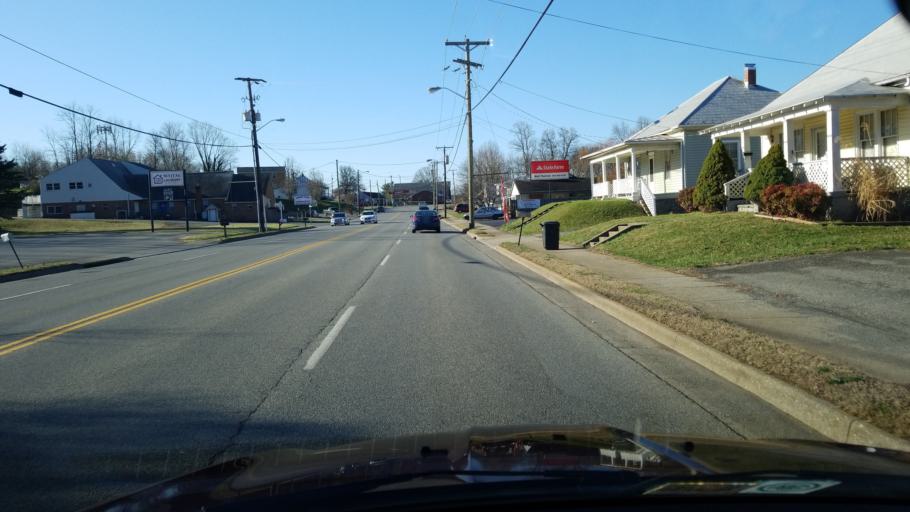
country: US
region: Virginia
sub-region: Franklin County
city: Rocky Mount
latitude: 37.0075
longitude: -79.8946
